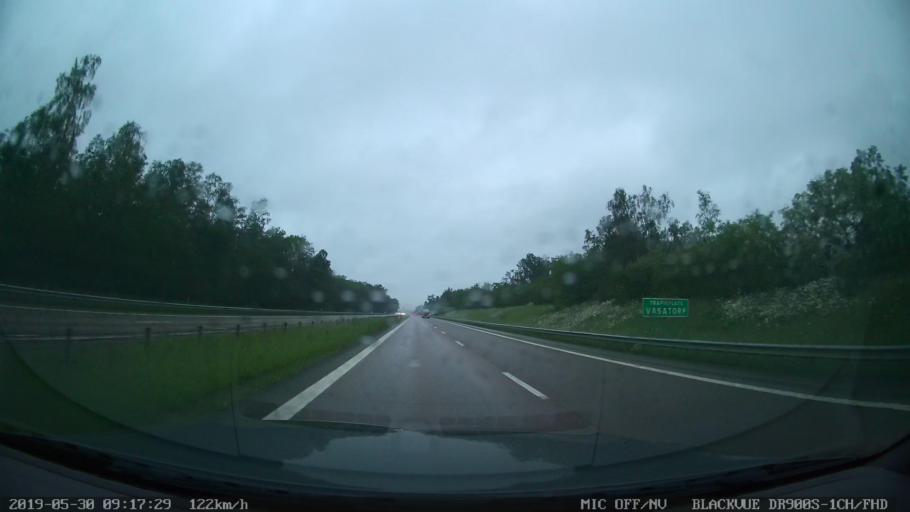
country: SE
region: Skane
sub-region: Helsingborg
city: Barslov
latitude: 56.0547
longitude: 12.7841
